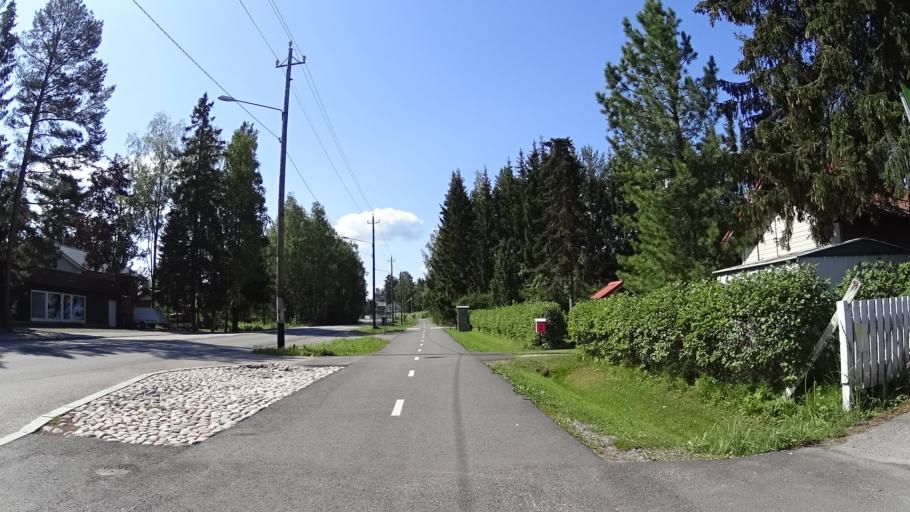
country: FI
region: Uusimaa
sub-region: Helsinki
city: Jaervenpaeae
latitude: 60.4674
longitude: 25.0681
